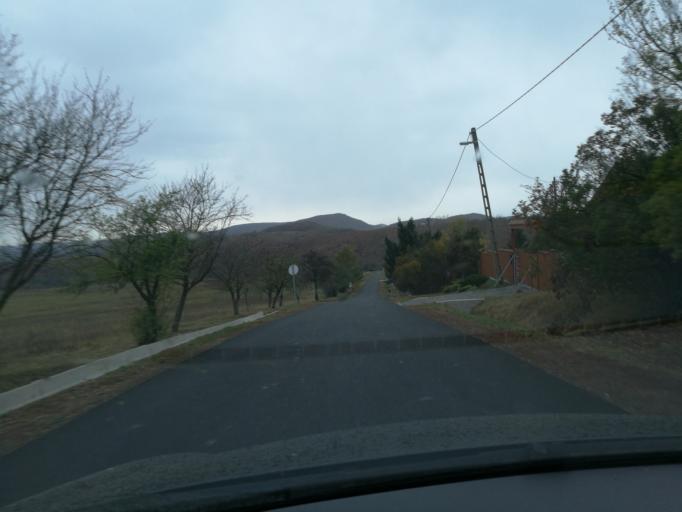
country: HU
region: Nograd
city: Paszto
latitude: 47.9766
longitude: 19.6383
